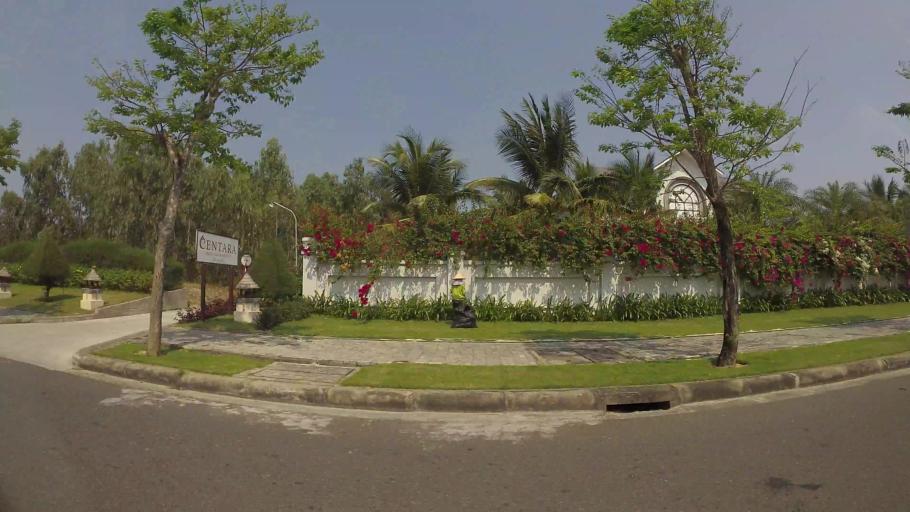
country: VN
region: Da Nang
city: Ngu Hanh Son
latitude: 15.9958
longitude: 108.2679
